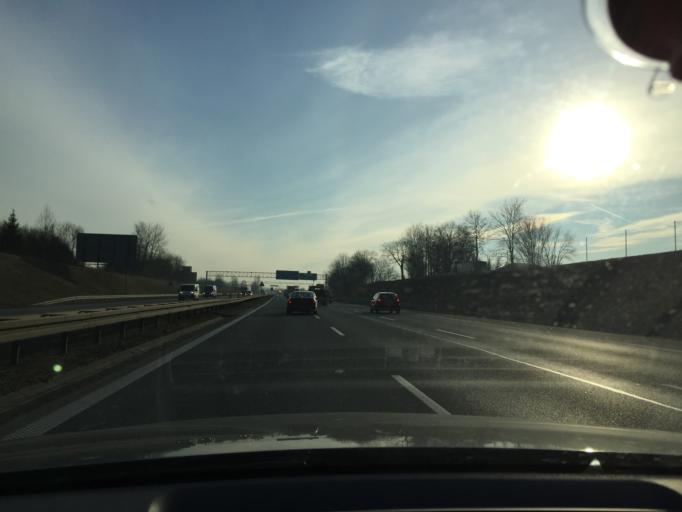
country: PL
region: Lesser Poland Voivodeship
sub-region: Powiat krakowski
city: Balice
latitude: 50.0795
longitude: 19.8084
